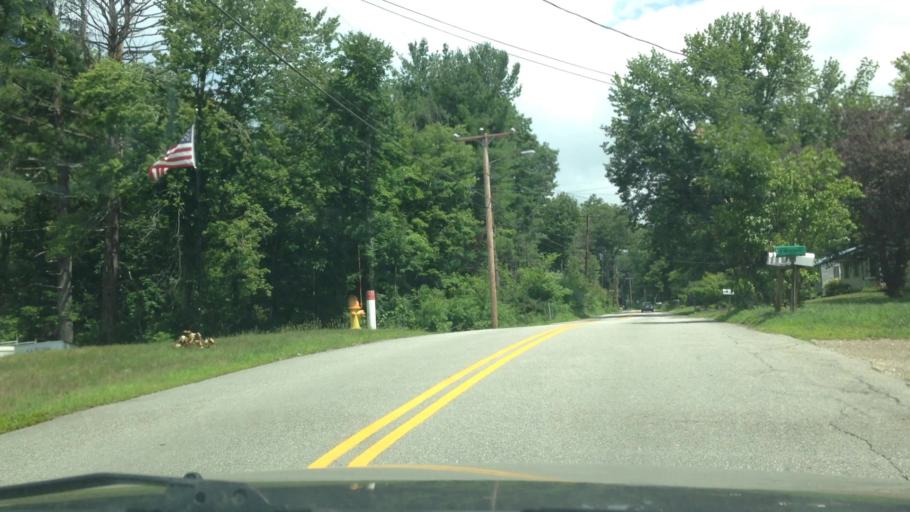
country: US
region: New Hampshire
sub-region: Cheshire County
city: Keene
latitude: 42.9096
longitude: -72.2560
